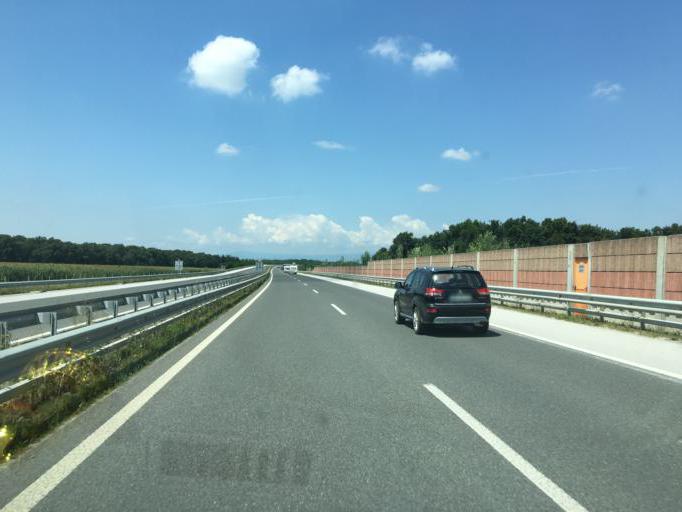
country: SI
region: Hajdina
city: Spodnja Hajdina
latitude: 46.3984
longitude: 15.8417
